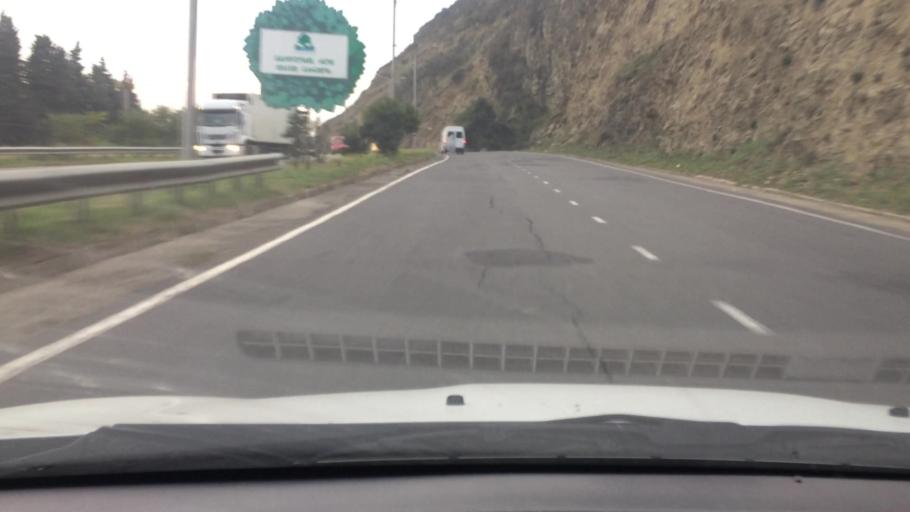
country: GE
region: T'bilisi
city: Tbilisi
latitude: 41.6588
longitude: 44.8899
